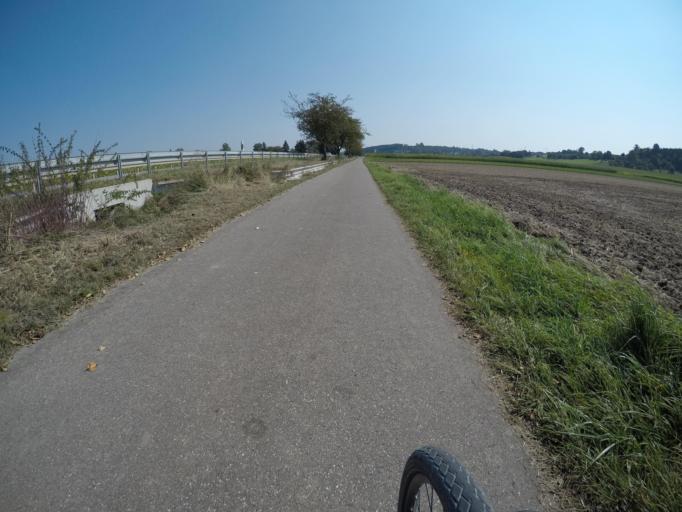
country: DE
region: Bavaria
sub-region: Swabia
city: Aislingen
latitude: 48.5109
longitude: 10.4373
